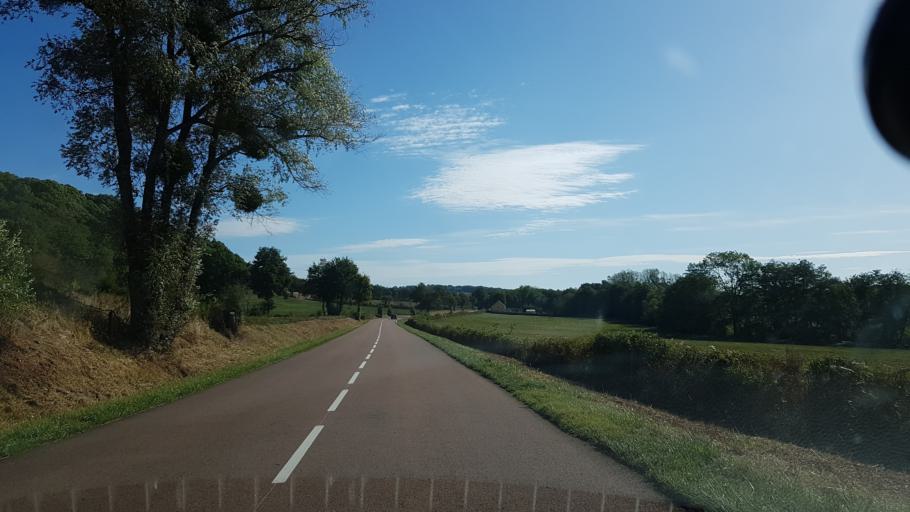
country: FR
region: Bourgogne
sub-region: Departement de la Nievre
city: Saint-Amand-en-Puisaye
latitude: 47.5369
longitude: 3.0114
